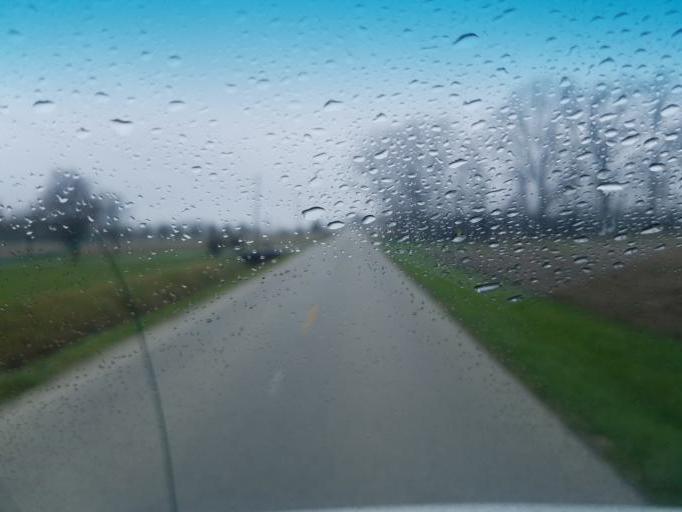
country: US
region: Ohio
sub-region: Hancock County
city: Findlay
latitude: 41.1166
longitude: -83.6443
